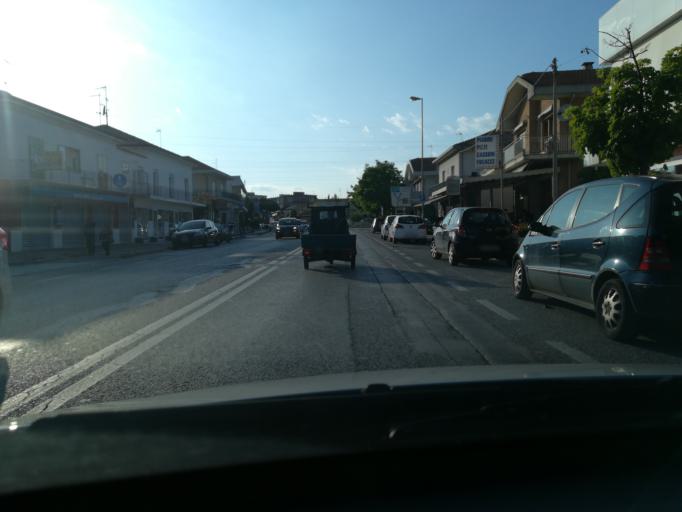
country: IT
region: Emilia-Romagna
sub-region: Provincia di Rimini
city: Riccione
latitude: 43.9920
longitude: 12.6639
